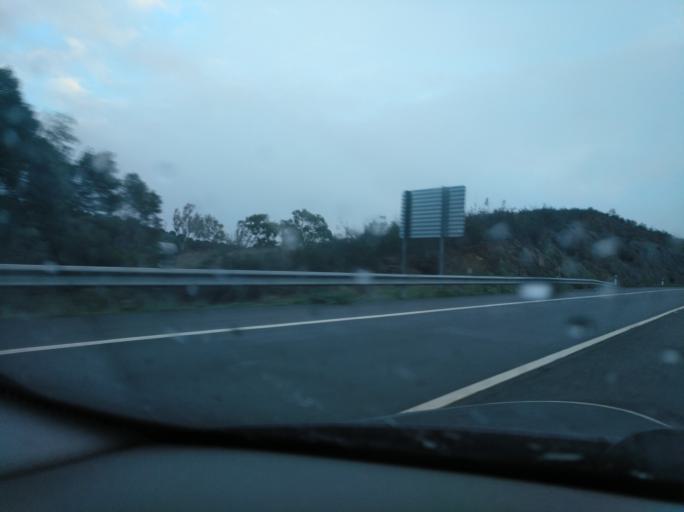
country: PT
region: Faro
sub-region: Castro Marim
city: Castro Marim
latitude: 37.3201
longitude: -7.4864
